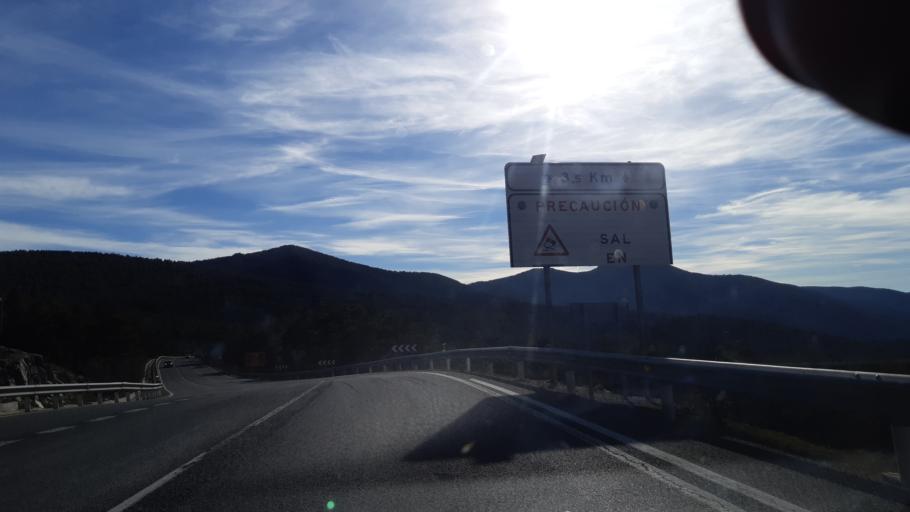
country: ES
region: Madrid
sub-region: Provincia de Madrid
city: Guadarrama
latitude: 40.7095
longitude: -4.1413
